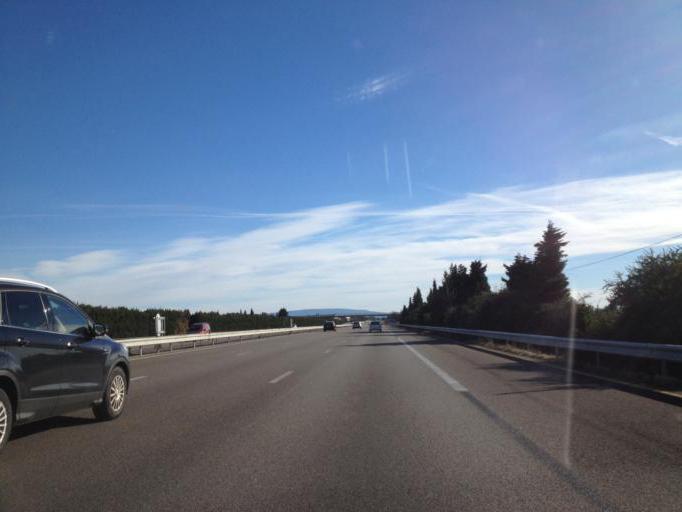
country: FR
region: Provence-Alpes-Cote d'Azur
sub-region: Departement du Vaucluse
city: Courthezon
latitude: 44.1033
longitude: 4.8599
